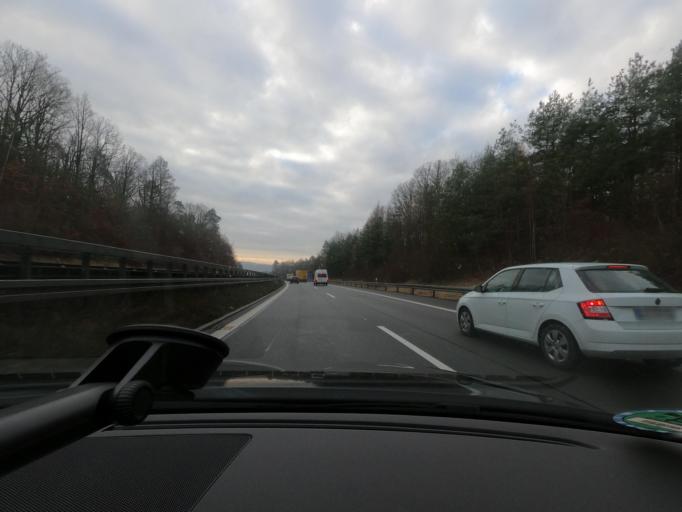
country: DE
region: Bavaria
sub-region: Upper Franconia
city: Zapfendorf
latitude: 50.0284
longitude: 10.9501
